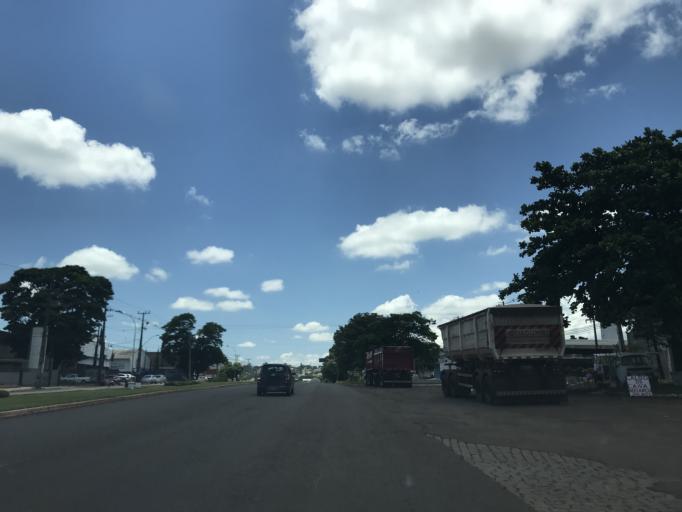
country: BR
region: Parana
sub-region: Marialva
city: Marialva
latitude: -23.4780
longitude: -51.8083
